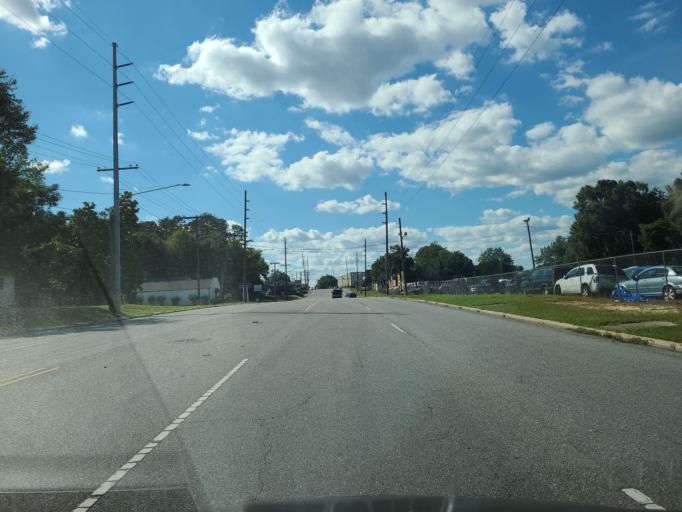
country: US
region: North Carolina
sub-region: Gaston County
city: Gastonia
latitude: 35.2572
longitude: -81.2041
